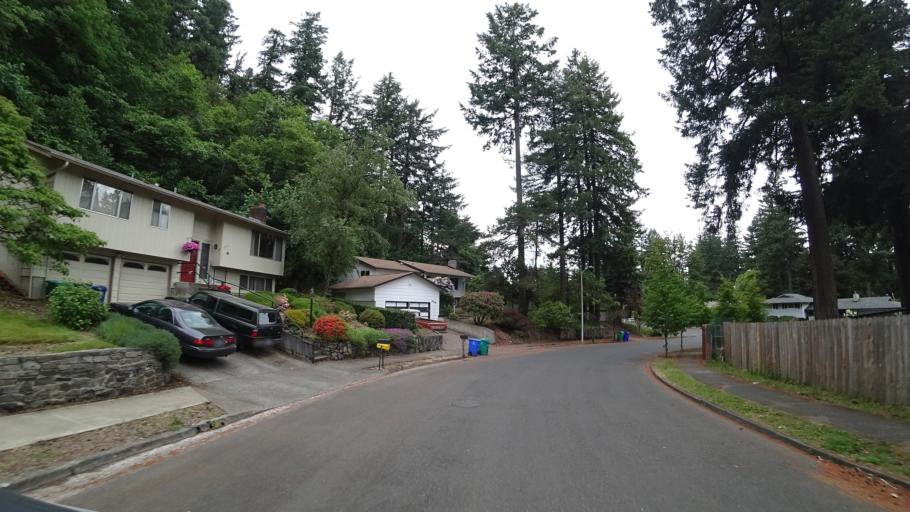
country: US
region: Oregon
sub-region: Clackamas County
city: Happy Valley
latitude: 45.4927
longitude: -122.5070
